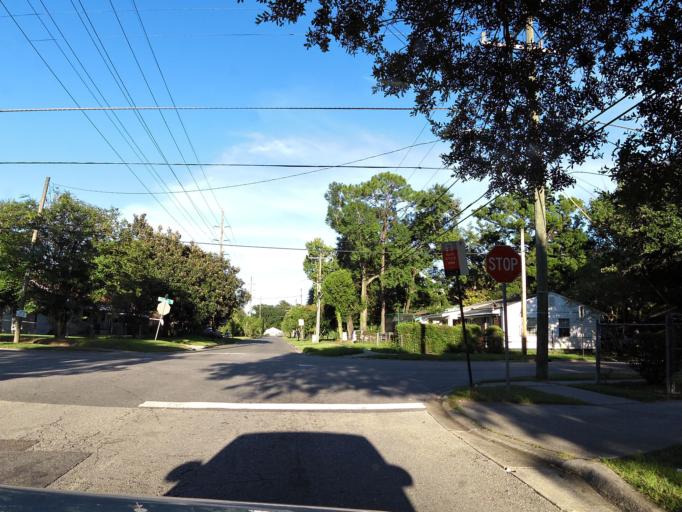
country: US
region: Florida
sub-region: Duval County
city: Jacksonville
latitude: 30.3595
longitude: -81.7017
